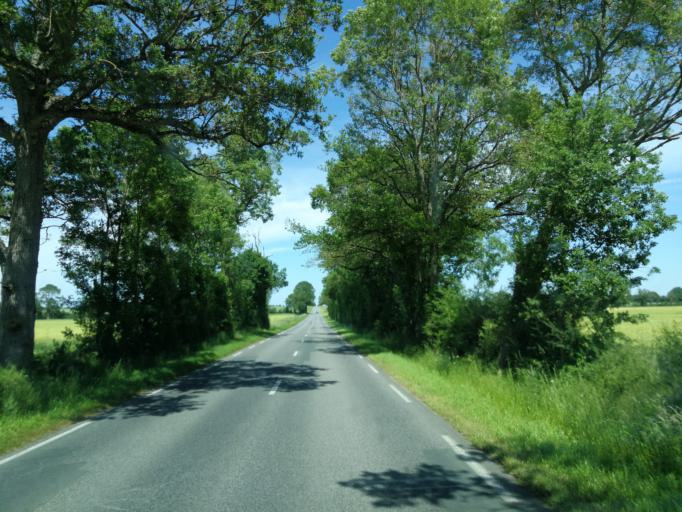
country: FR
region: Poitou-Charentes
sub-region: Departement des Deux-Sevres
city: Saint-Varent
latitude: 46.8894
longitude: -0.3075
